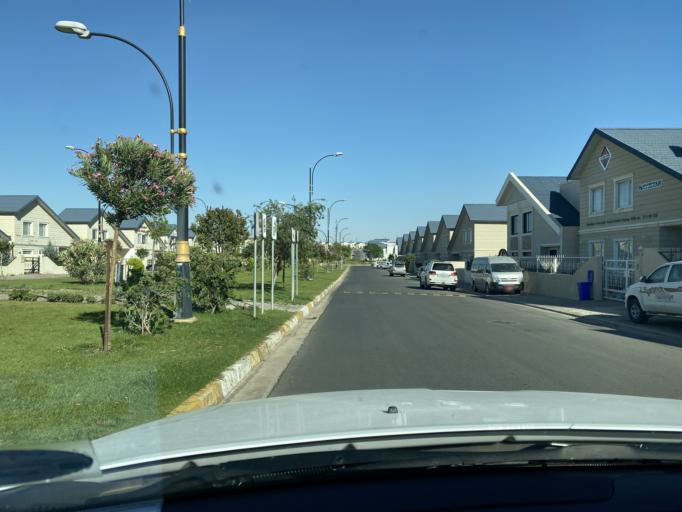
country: IQ
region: Arbil
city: Erbil
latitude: 36.2426
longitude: 44.0490
